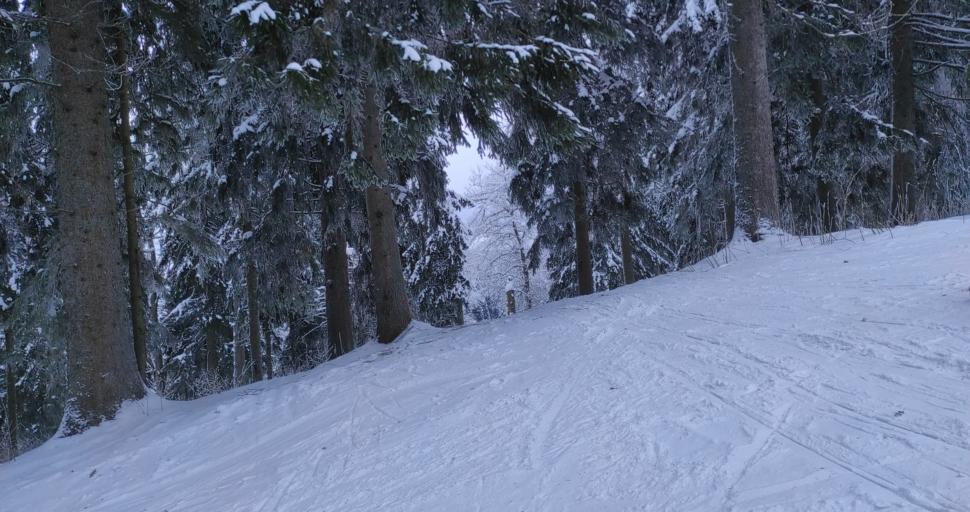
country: LV
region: Vecpiebalga
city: Vecpiebalga
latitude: 56.8745
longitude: 25.9620
